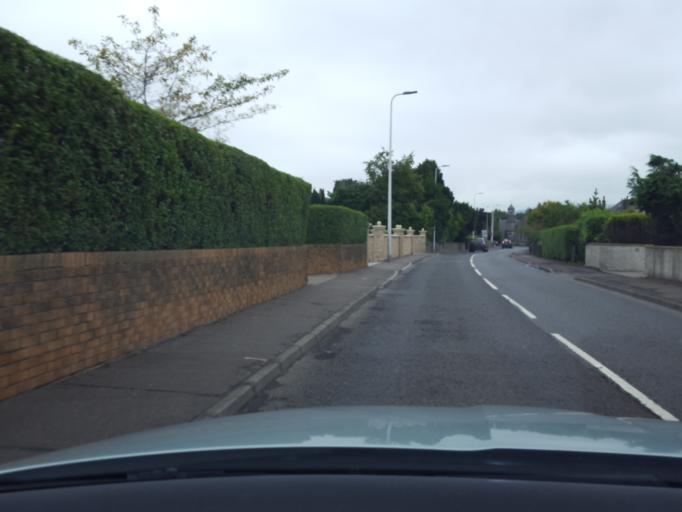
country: GB
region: Scotland
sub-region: Perth and Kinross
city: Kinross
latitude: 56.2110
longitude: -3.4283
